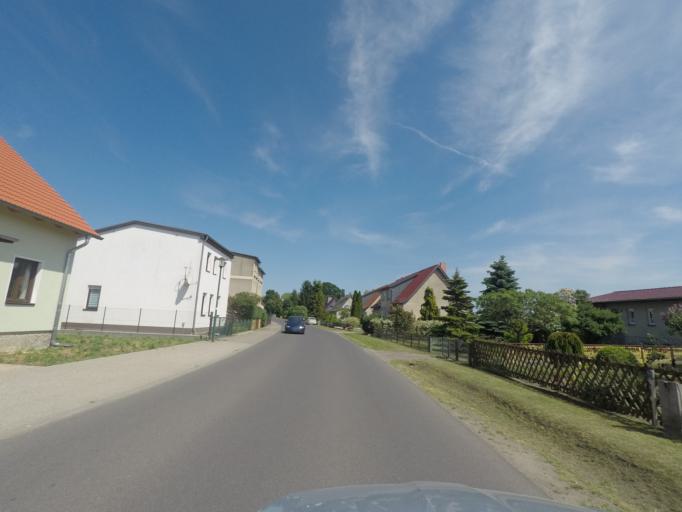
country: DE
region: Brandenburg
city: Britz
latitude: 52.8681
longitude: 13.7540
